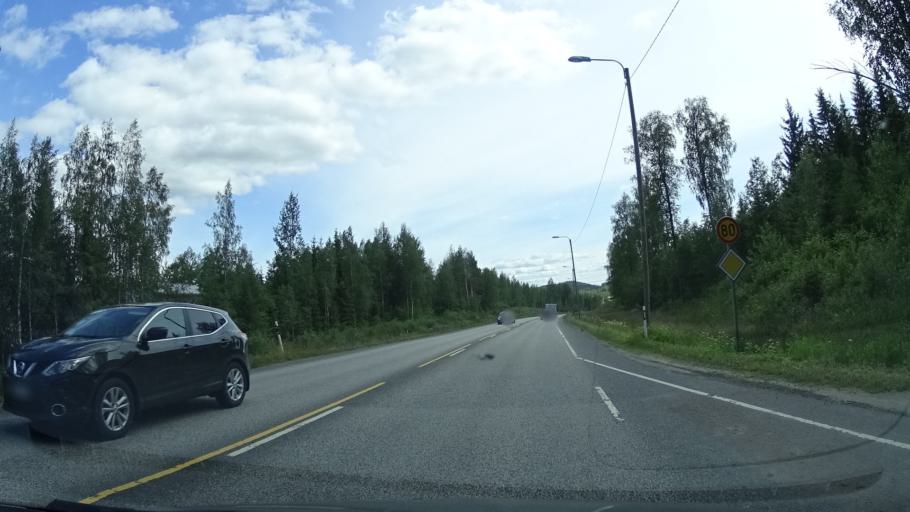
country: FI
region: Central Finland
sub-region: Jyvaeskylae
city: Jyvaeskylae
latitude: 62.2601
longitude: 25.6013
